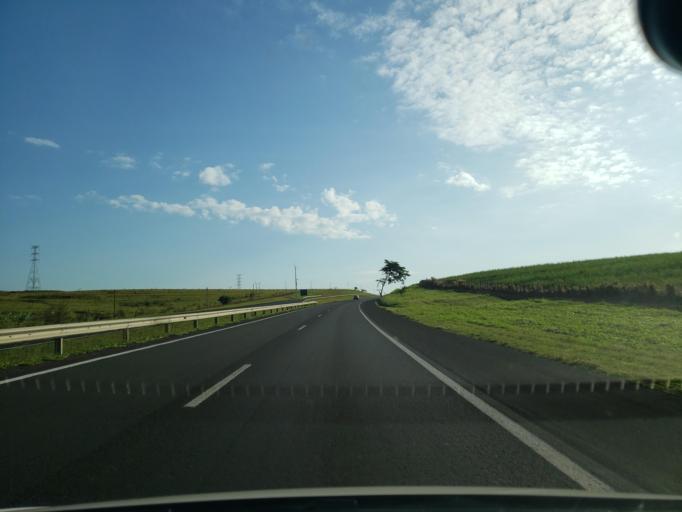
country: BR
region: Sao Paulo
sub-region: Valparaiso
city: Valparaiso
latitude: -21.2172
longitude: -50.8433
